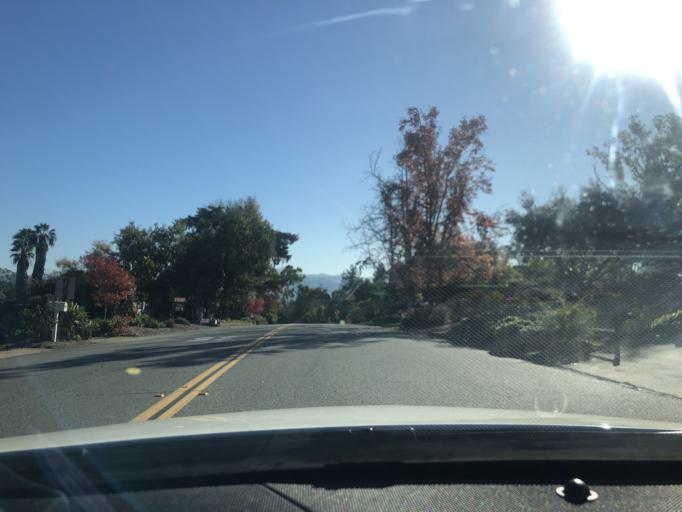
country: US
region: California
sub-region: San Diego County
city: Casa de Oro-Mount Helix
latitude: 32.7701
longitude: -116.9475
